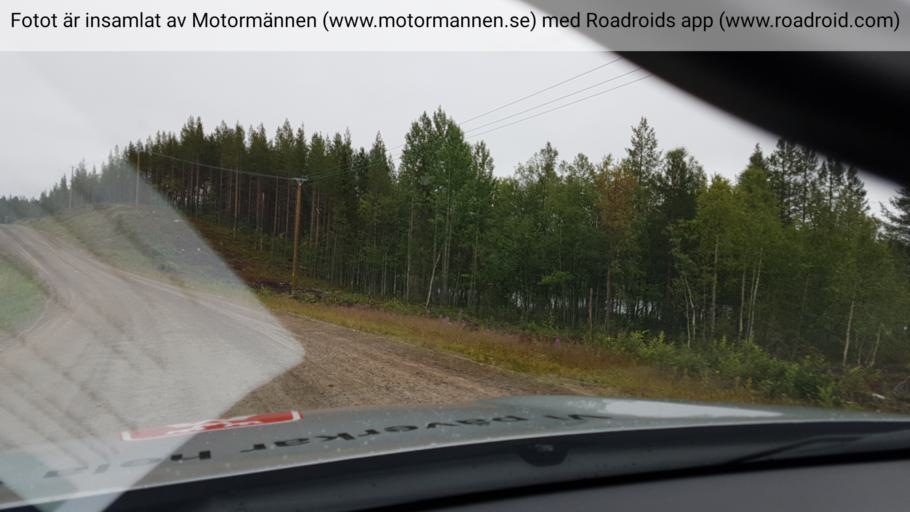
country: SE
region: Norrbotten
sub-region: Gallivare Kommun
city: Gaellivare
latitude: 66.7211
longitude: 20.5386
